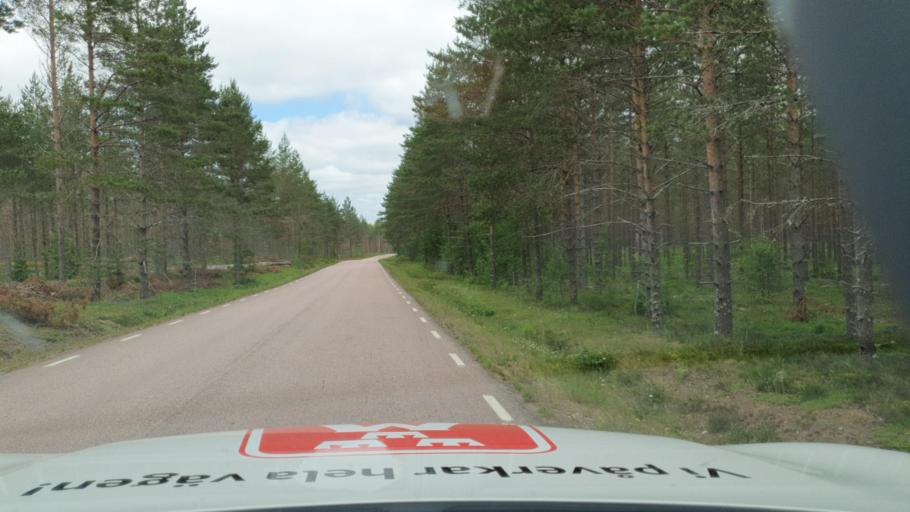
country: SE
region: Vaermland
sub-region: Filipstads Kommun
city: Filipstad
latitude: 59.6421
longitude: 13.9998
